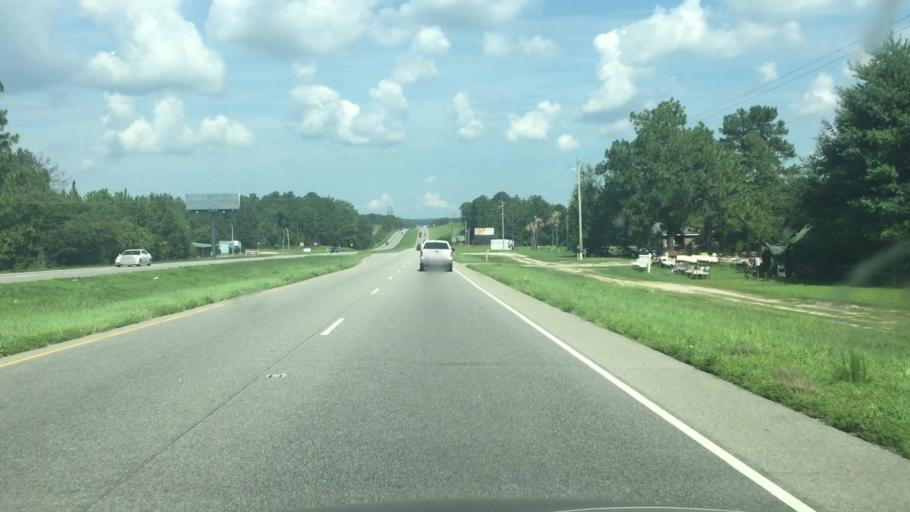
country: US
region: North Carolina
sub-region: Scotland County
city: Laurel Hill
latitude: 34.8435
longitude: -79.6070
